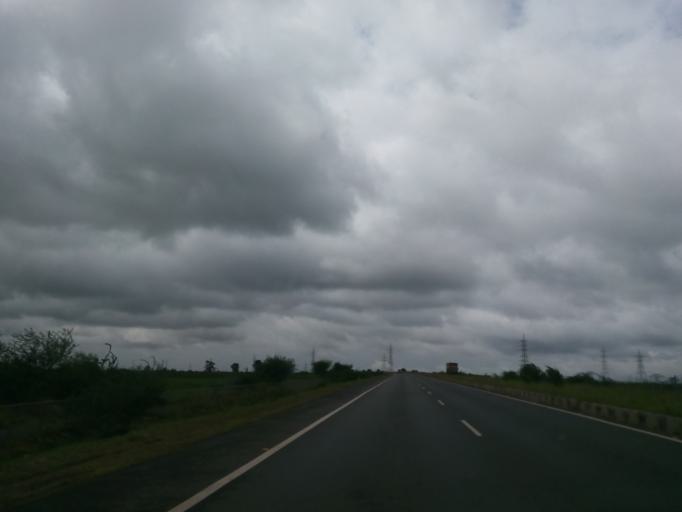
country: IN
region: Karnataka
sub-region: Haveri
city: Haveri
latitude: 14.8175
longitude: 75.3708
